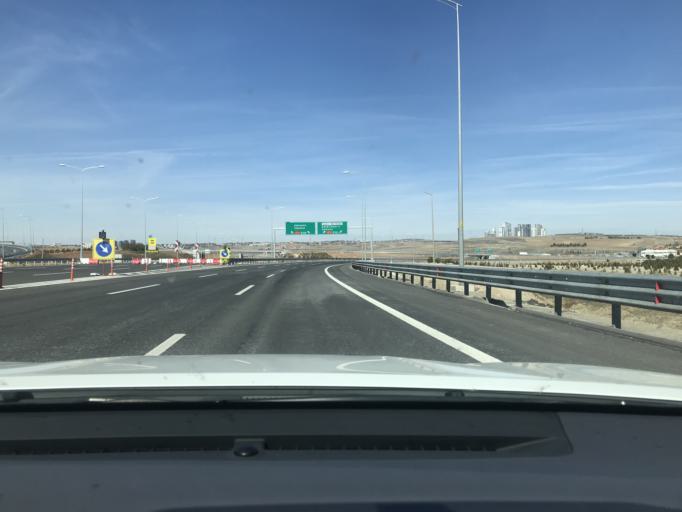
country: TR
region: Ankara
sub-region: Goelbasi
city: Golbasi
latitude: 39.7821
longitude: 32.7448
